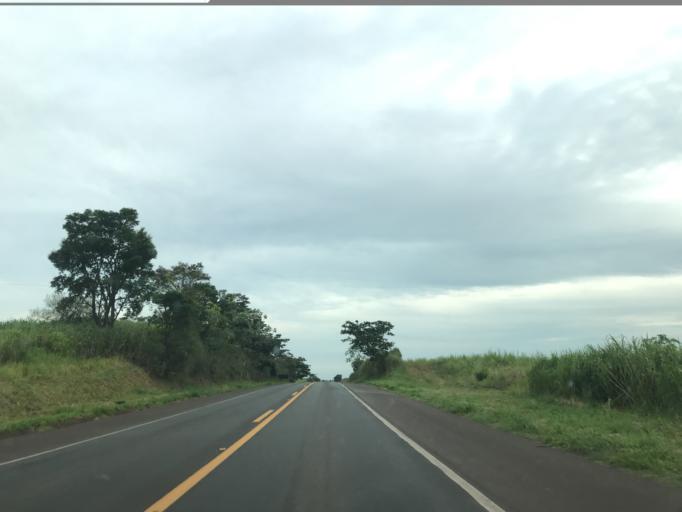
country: BR
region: Sao Paulo
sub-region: Birigui
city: Birigui
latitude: -21.5817
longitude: -50.4529
